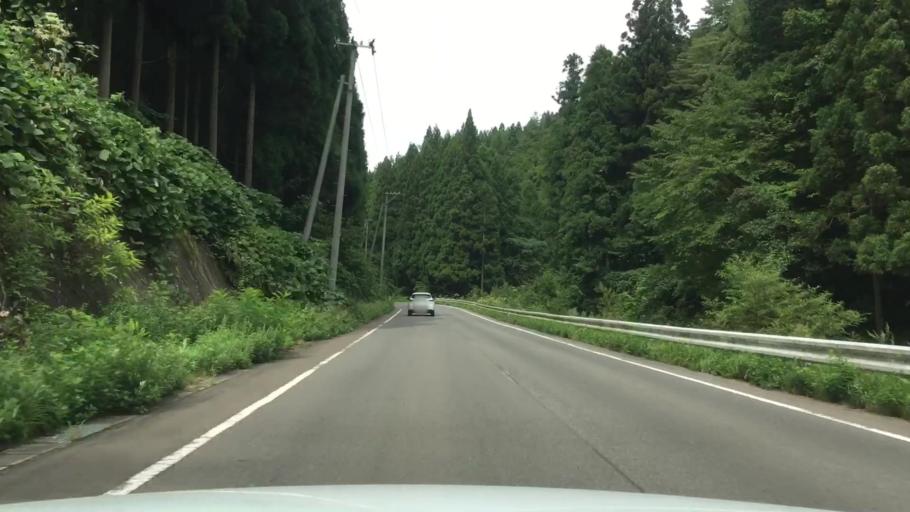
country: JP
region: Aomori
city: Shimokizukuri
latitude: 40.7374
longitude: 140.2480
